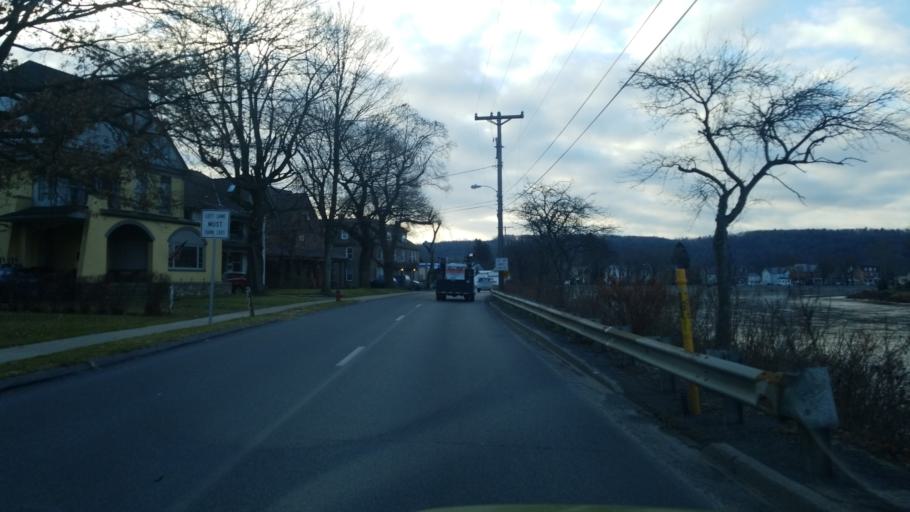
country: US
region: Pennsylvania
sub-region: Clearfield County
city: Clearfield
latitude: 41.0191
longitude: -78.4396
